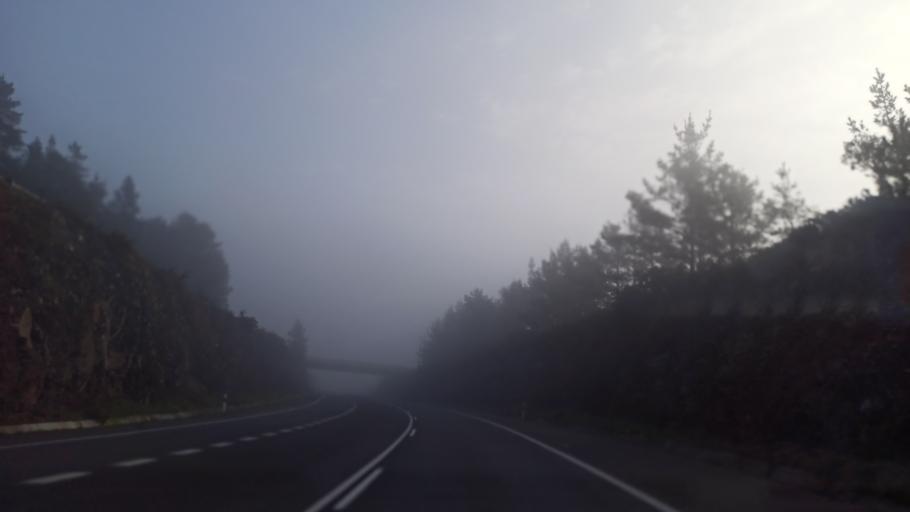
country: ES
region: Galicia
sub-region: Provincia da Coruna
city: As Pontes de Garcia Rodriguez
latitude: 43.4409
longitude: -7.9388
